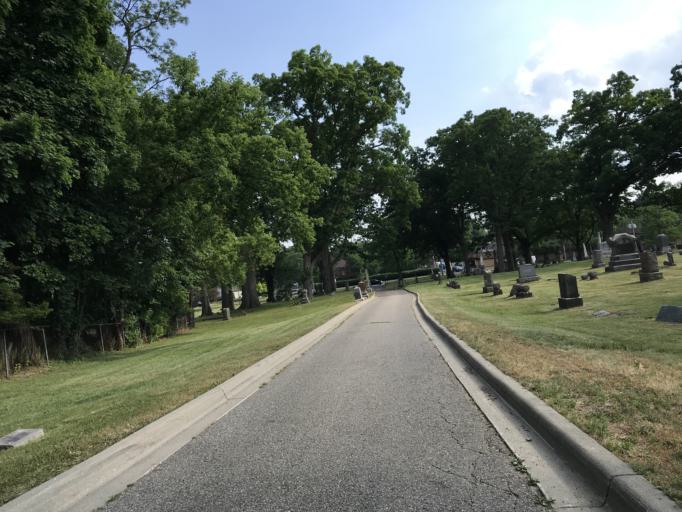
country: US
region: Michigan
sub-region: Oakland County
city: Farmington
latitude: 42.4699
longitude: -83.3848
